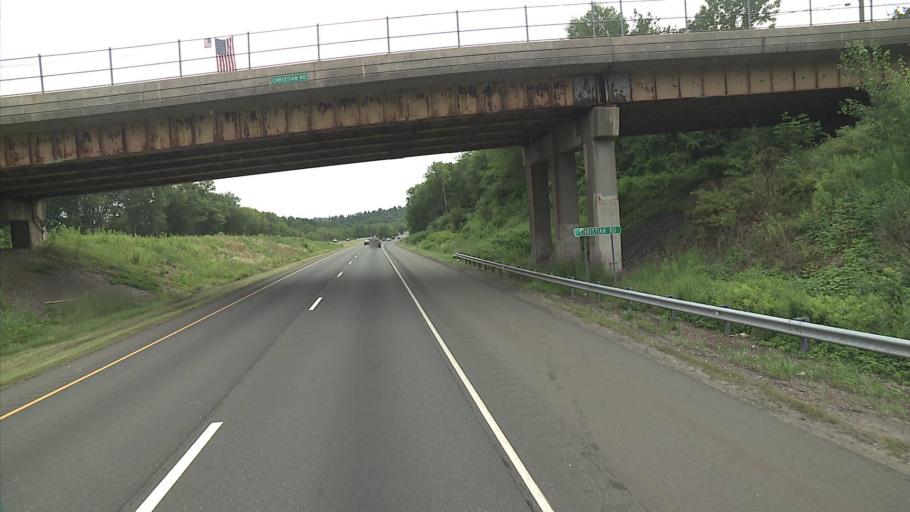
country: US
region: Connecticut
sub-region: New Haven County
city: Middlebury
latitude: 41.5069
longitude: -73.1417
